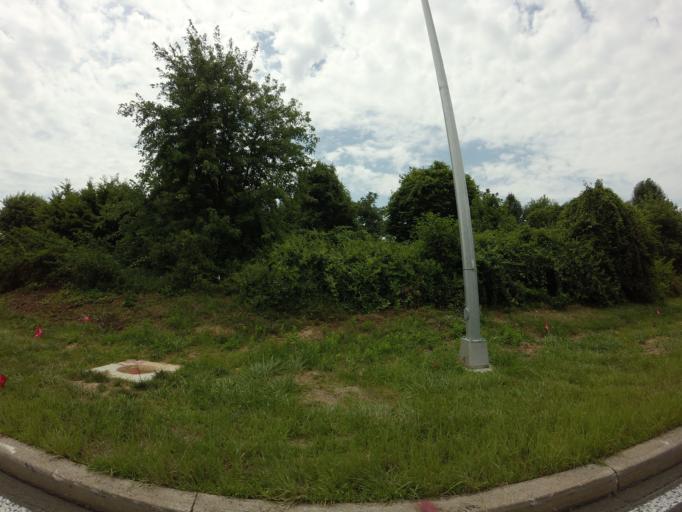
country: US
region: Maryland
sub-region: Baltimore County
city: Hunt Valley
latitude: 39.4962
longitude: -76.6678
